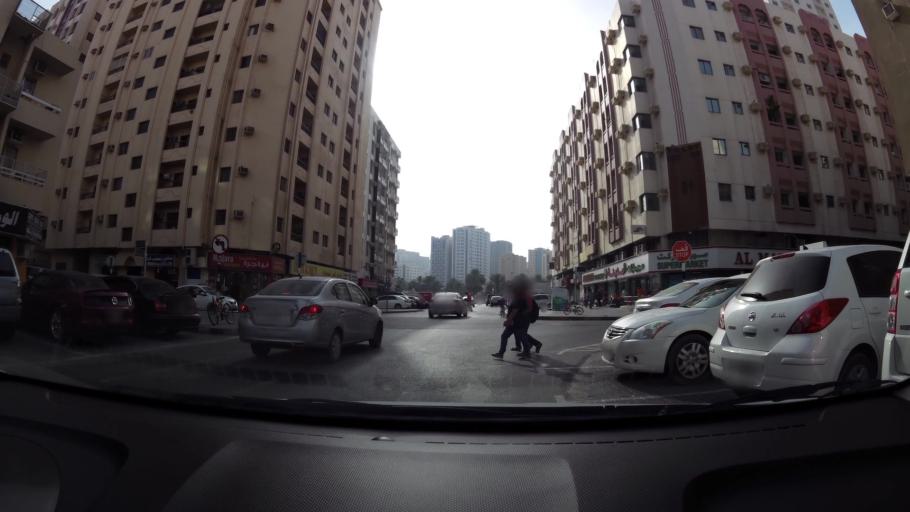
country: AE
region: Ash Shariqah
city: Sharjah
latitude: 25.3347
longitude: 55.3975
